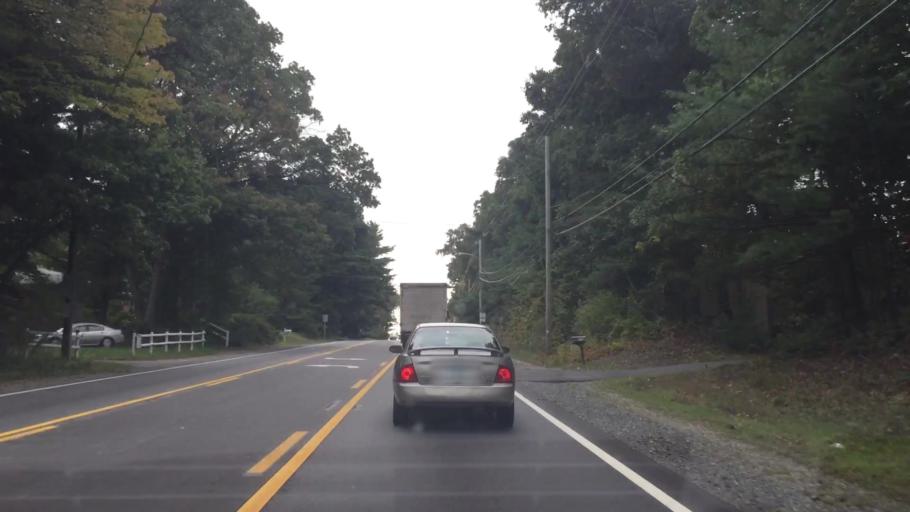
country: US
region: Massachusetts
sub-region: Middlesex County
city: North Reading
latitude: 42.6274
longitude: -71.0622
